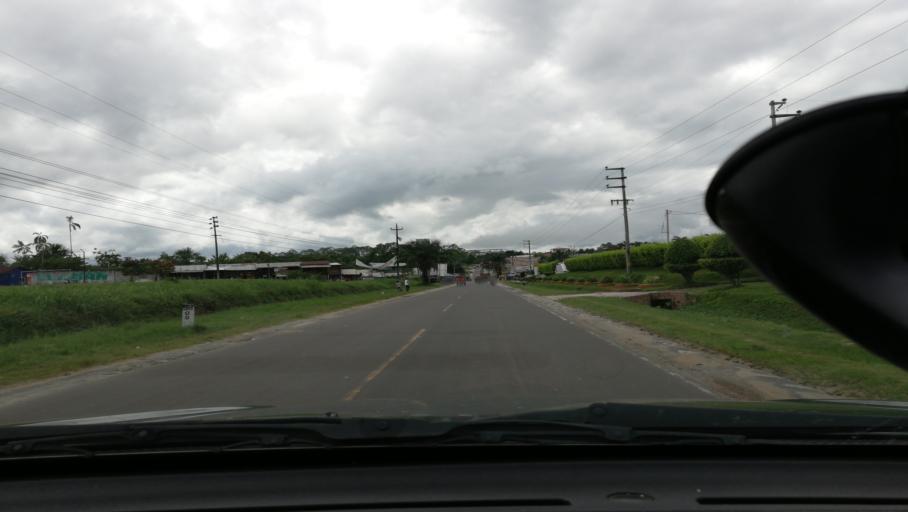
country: PE
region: Loreto
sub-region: Provincia de Maynas
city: Iquitos
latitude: -3.8477
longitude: -73.3376
